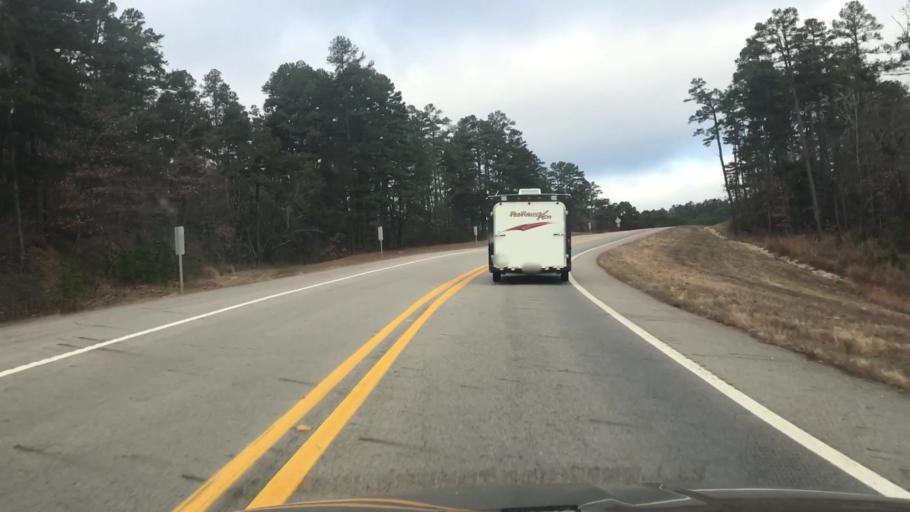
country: US
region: Arkansas
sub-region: Montgomery County
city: Mount Ida
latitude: 34.6795
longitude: -93.7870
